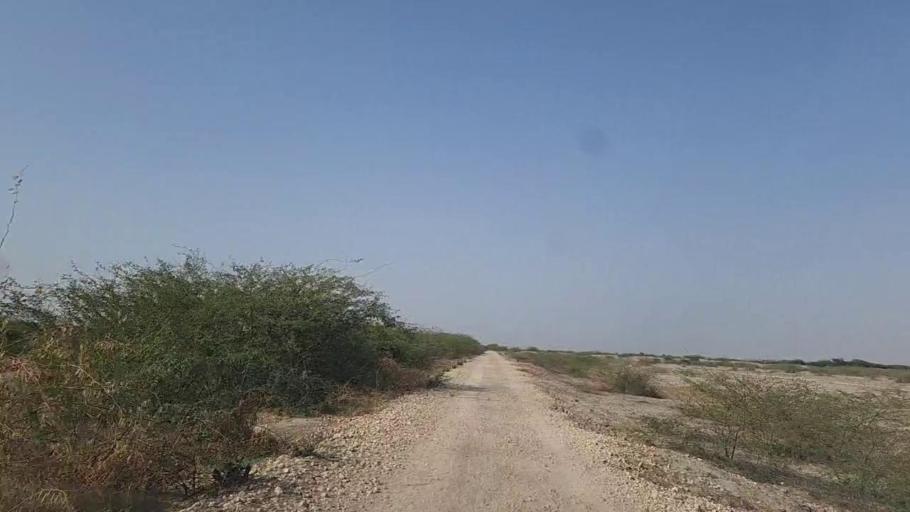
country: PK
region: Sindh
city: Naukot
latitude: 24.6068
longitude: 69.2747
